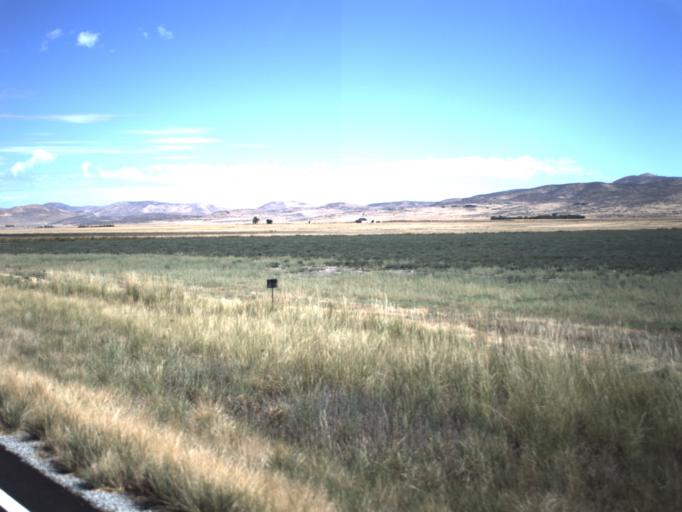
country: US
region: Utah
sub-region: Box Elder County
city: Tremonton
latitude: 41.7407
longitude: -112.4342
